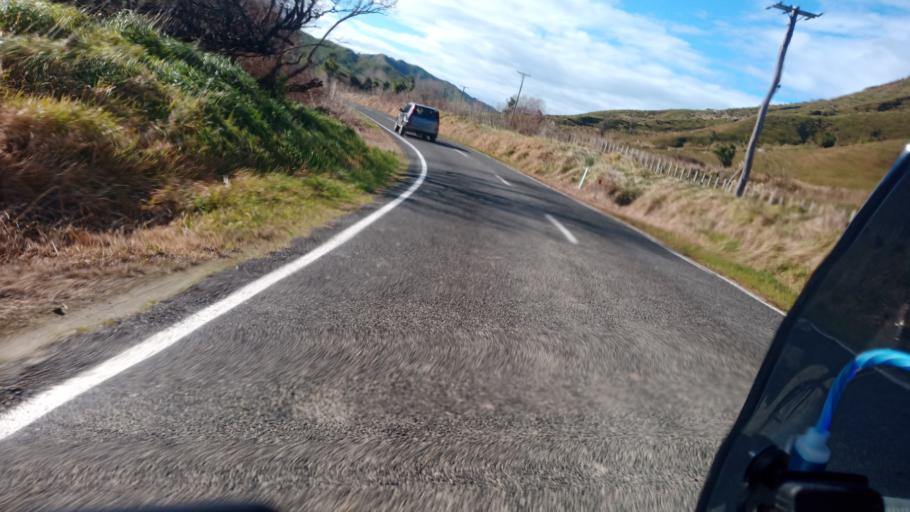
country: NZ
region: Gisborne
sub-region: Gisborne District
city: Gisborne
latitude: -38.2739
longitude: 178.2711
